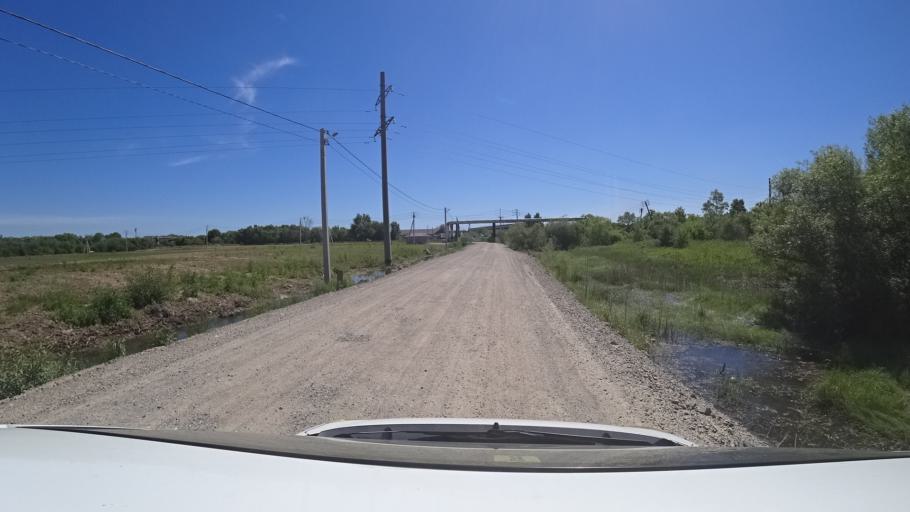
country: RU
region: Khabarovsk Krai
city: Topolevo
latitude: 48.4759
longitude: 135.1716
